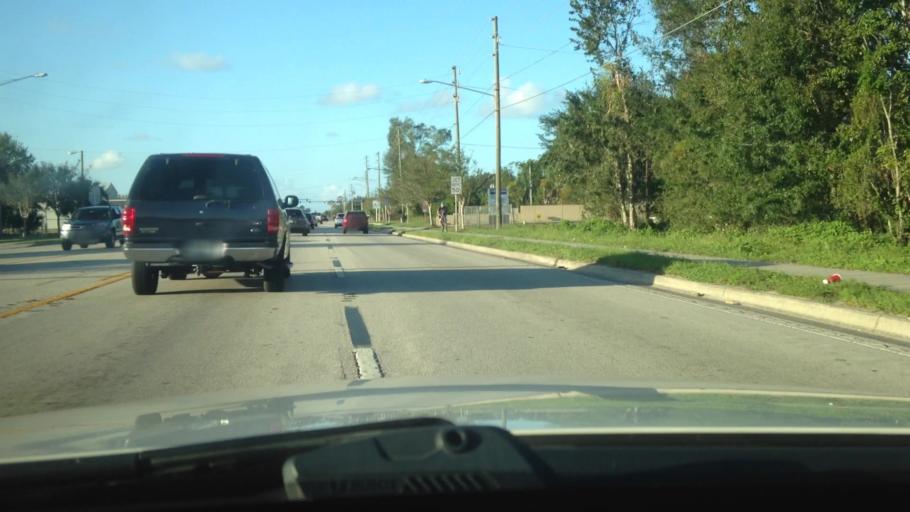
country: US
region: Florida
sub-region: Orange County
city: Union Park
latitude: 28.5652
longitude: -81.2860
